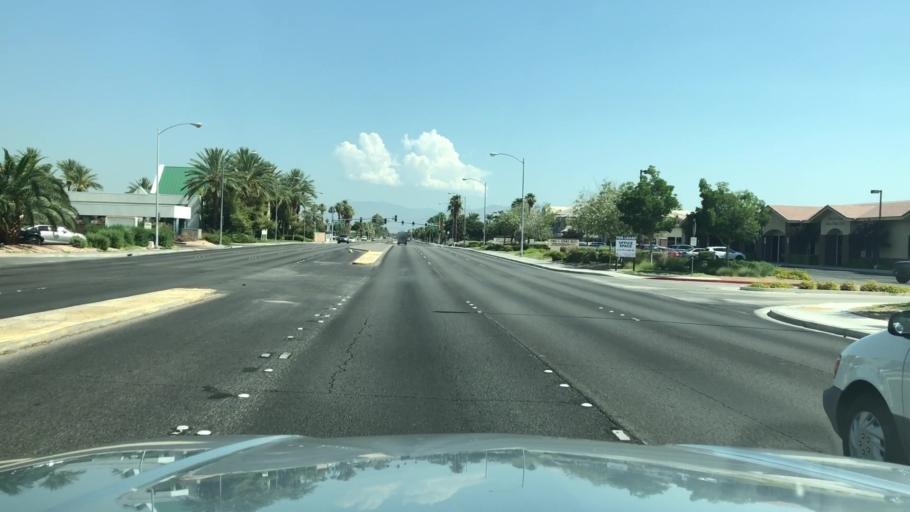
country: US
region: Nevada
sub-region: Clark County
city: Spring Valley
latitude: 36.1345
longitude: -115.2250
